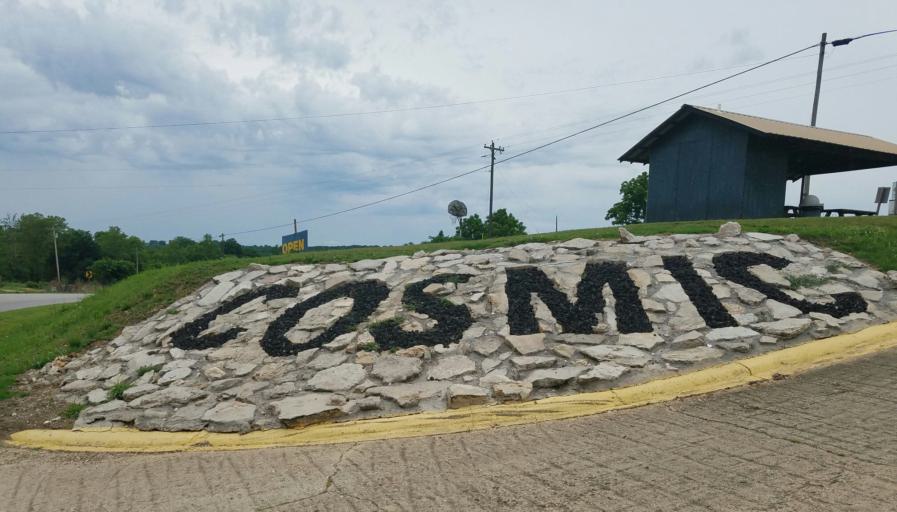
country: US
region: Arkansas
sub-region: Carroll County
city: Berryville
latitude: 36.4348
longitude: -93.4981
